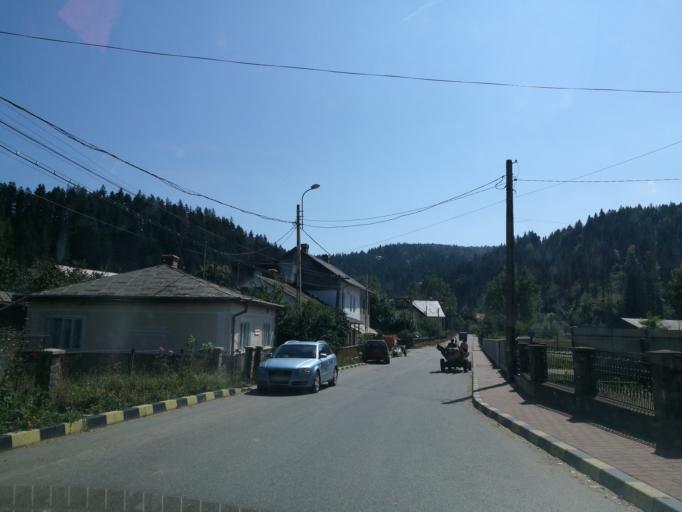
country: RO
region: Suceava
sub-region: Comuna Putna
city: Putna
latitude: 47.8686
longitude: 25.6120
